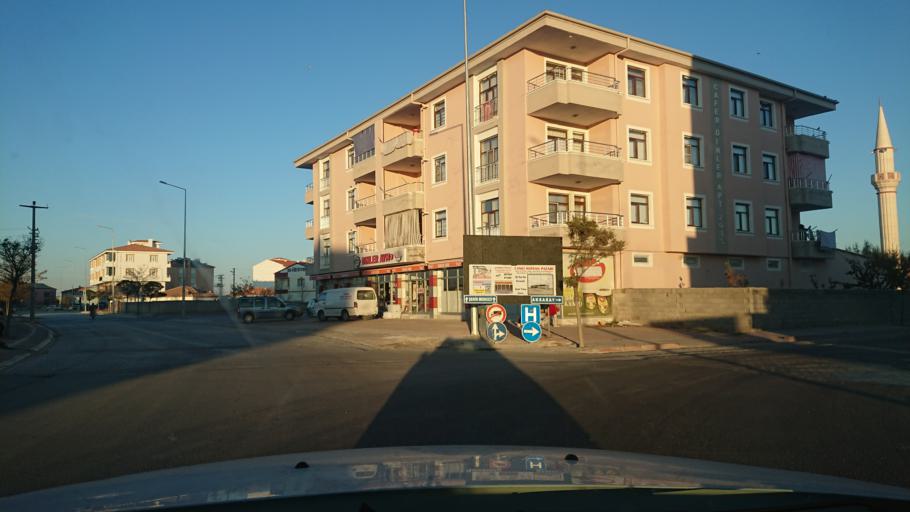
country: TR
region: Aksaray
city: Eskil
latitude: 38.4000
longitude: 33.4062
